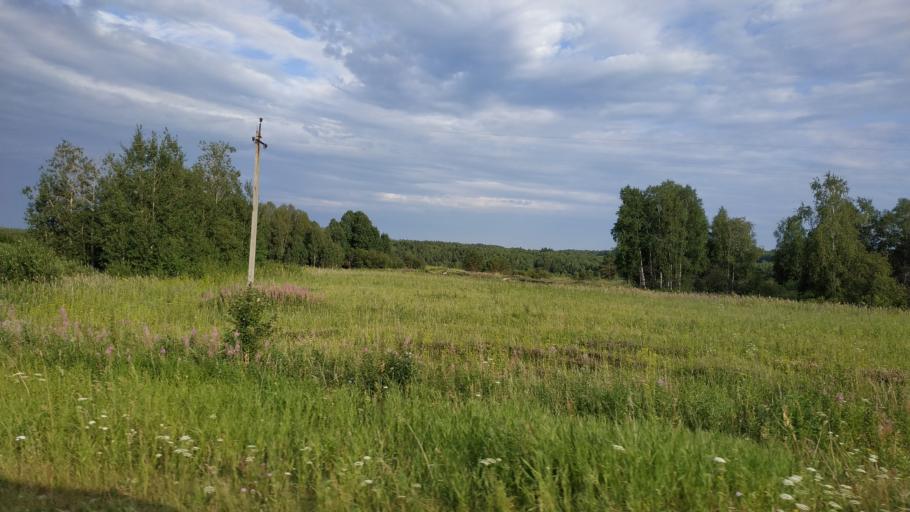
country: RU
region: Sverdlovsk
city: Yelanskiy
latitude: 57.0712
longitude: 62.4381
